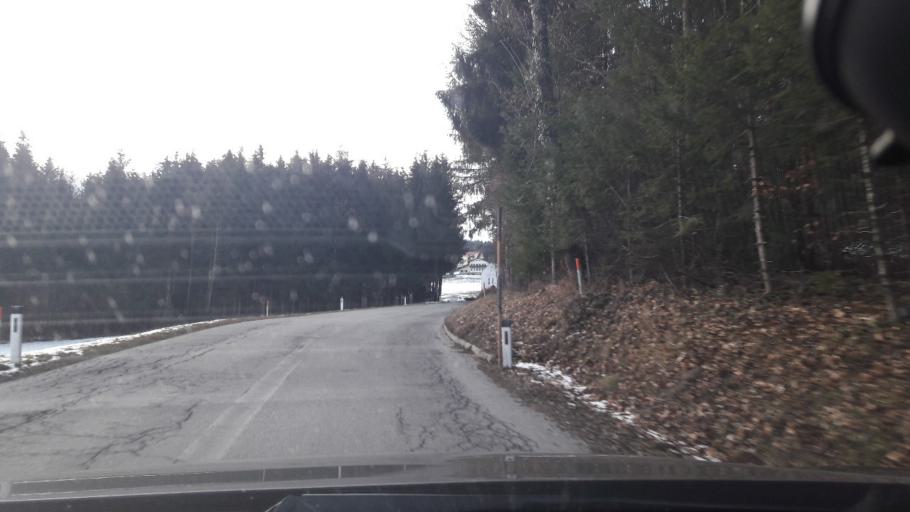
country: AT
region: Styria
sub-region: Politischer Bezirk Graz-Umgebung
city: Sankt Bartholoma
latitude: 47.0741
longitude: 15.2592
